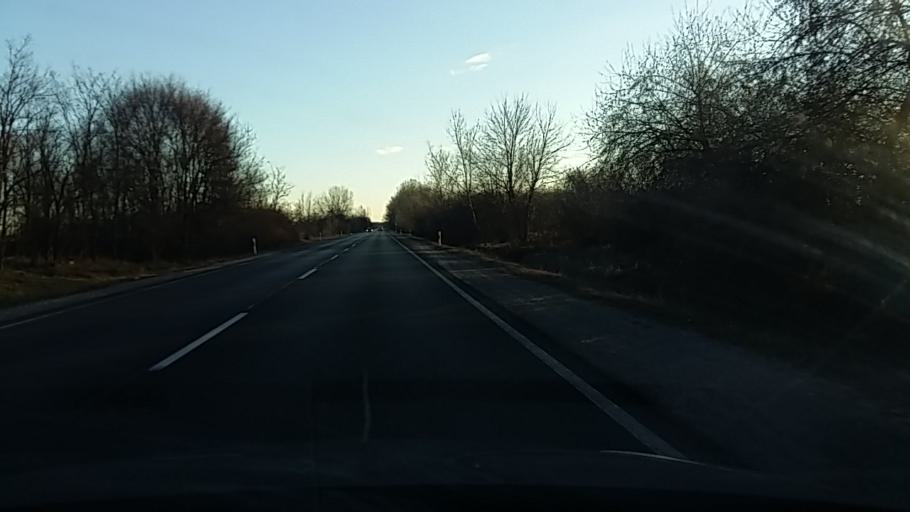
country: HU
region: Szabolcs-Szatmar-Bereg
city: Ujfeherto
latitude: 47.8458
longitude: 21.7043
